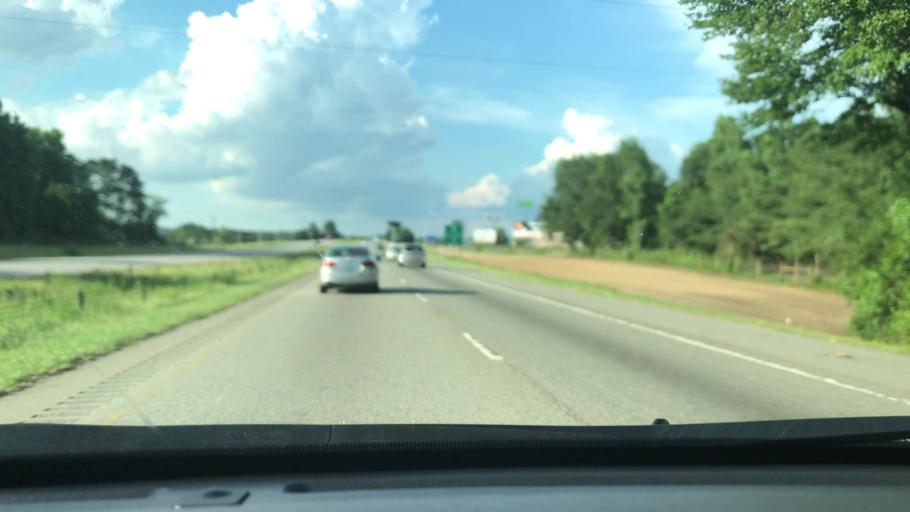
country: US
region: North Carolina
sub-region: Robeson County
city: Saint Pauls
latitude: 34.8053
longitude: -78.9887
